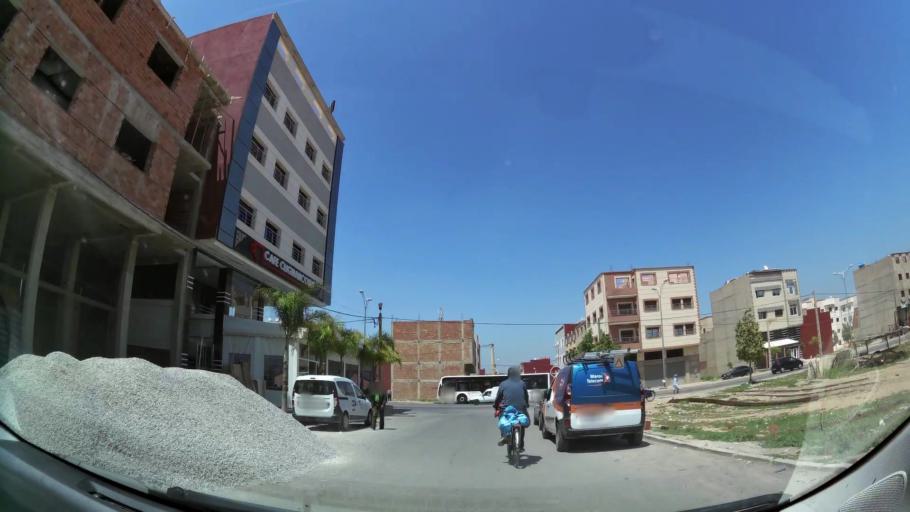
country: MA
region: Oriental
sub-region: Oujda-Angad
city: Oujda
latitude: 34.6963
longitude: -1.8873
